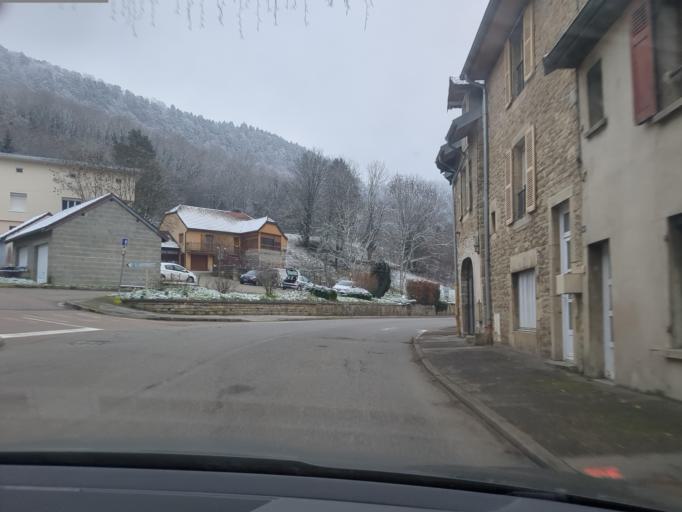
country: FR
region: Franche-Comte
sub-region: Departement du Jura
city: Perrigny
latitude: 46.6532
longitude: 5.5998
